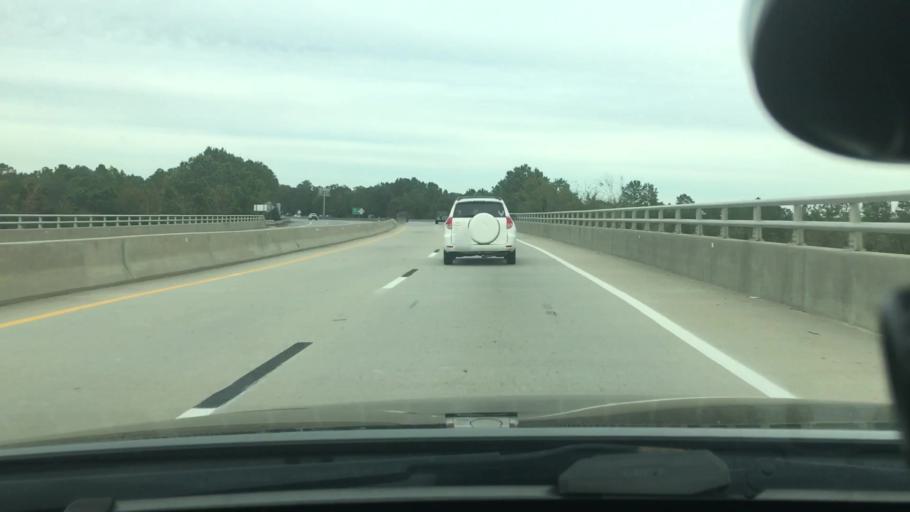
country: US
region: North Carolina
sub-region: Craven County
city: James City
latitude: 35.1019
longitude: -77.0116
